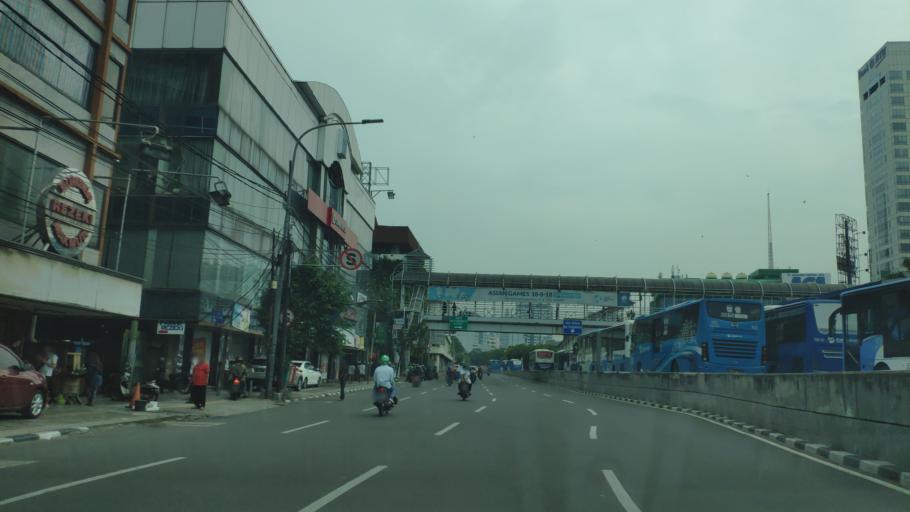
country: ID
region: Jakarta Raya
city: Jakarta
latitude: -6.1652
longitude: 106.8205
